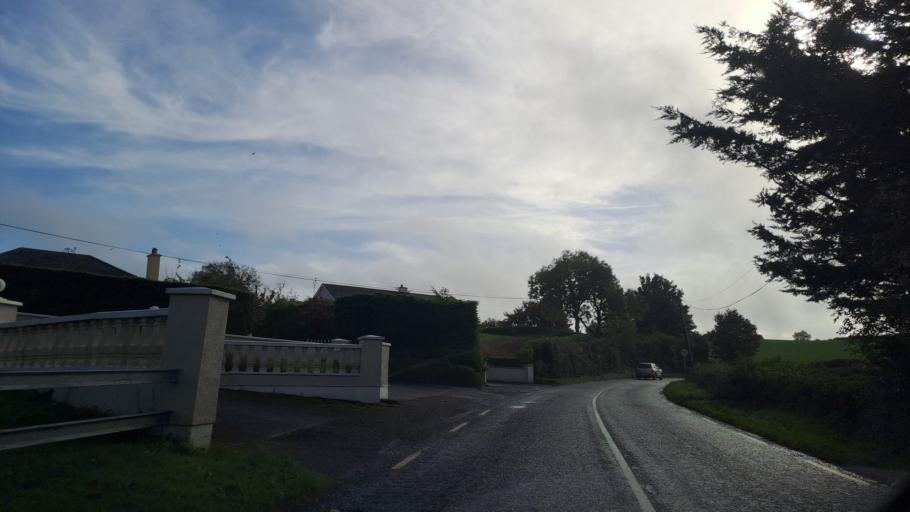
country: IE
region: Ulster
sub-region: County Monaghan
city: Carrickmacross
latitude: 53.9570
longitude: -6.7115
